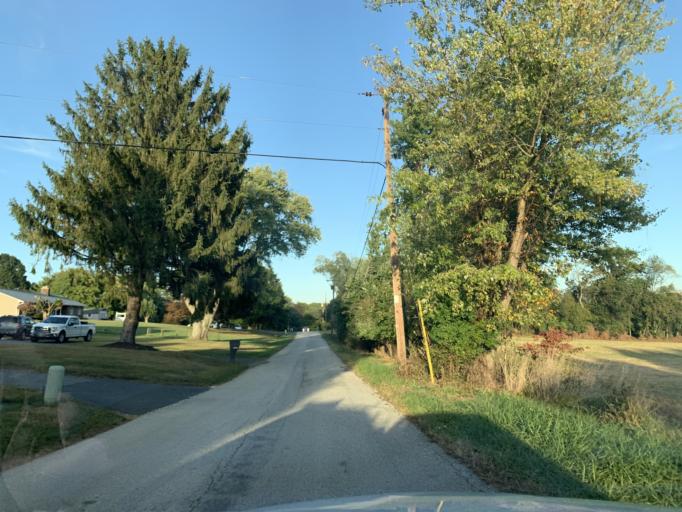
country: US
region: Maryland
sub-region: Harford County
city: Fallston
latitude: 39.4874
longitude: -76.4449
